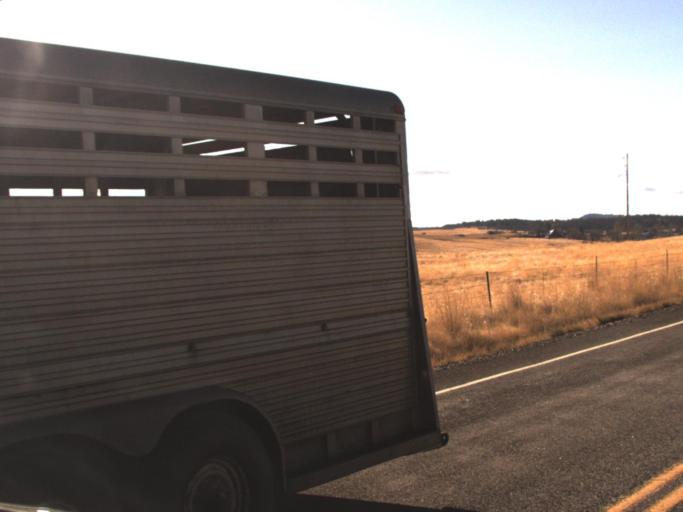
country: US
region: Washington
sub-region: Asotin County
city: Asotin
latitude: 46.1490
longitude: -117.1216
